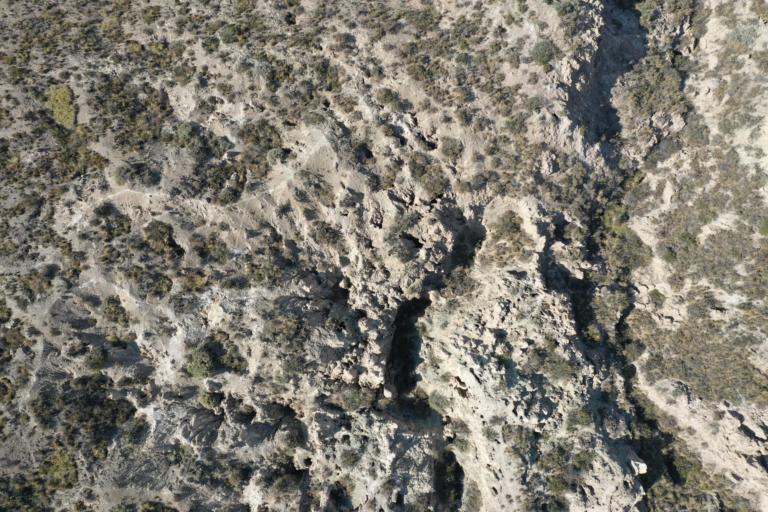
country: BO
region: La Paz
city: La Paz
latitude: -16.5616
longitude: -68.1239
